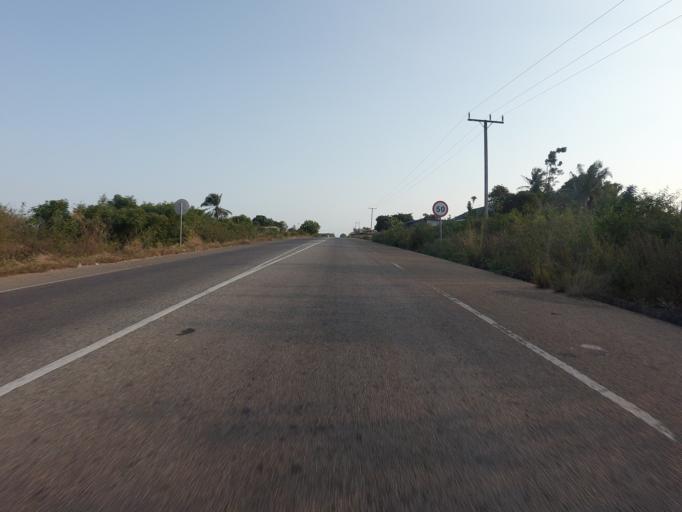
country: GH
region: Volta
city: Anloga
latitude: 6.0185
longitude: 0.5995
